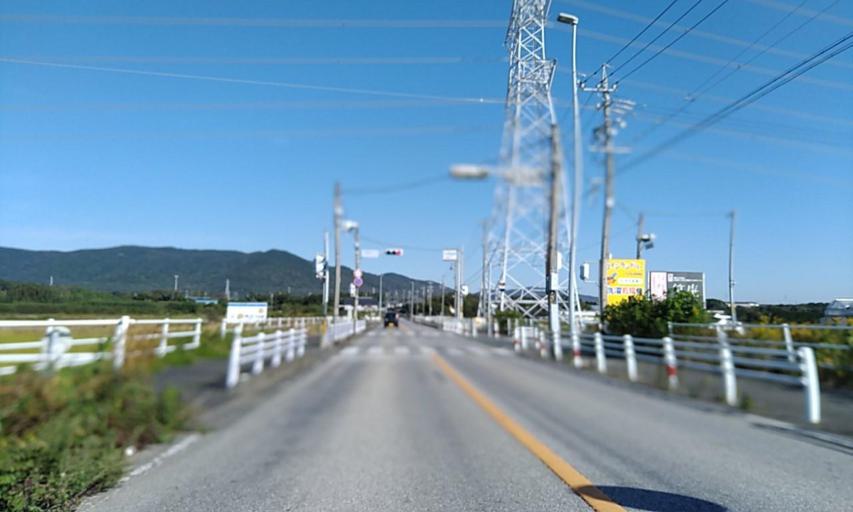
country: JP
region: Aichi
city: Tahara
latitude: 34.6390
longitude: 137.2384
